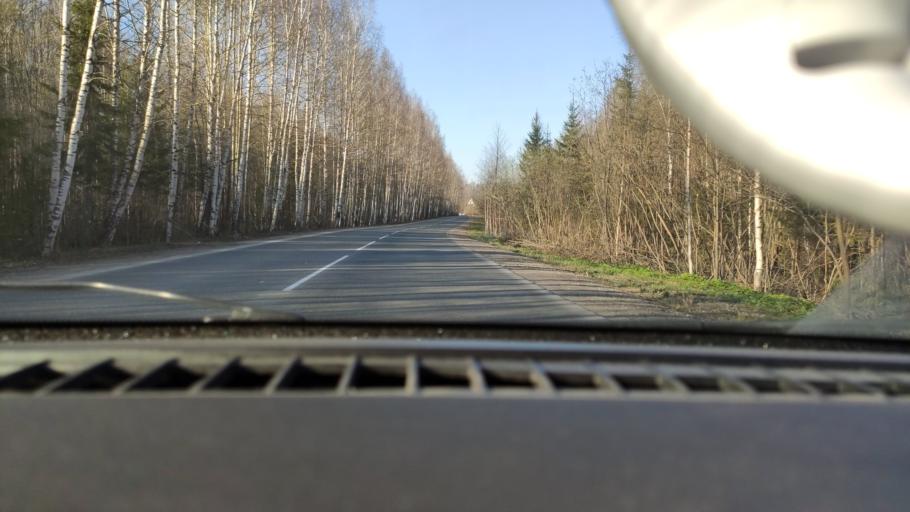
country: RU
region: Perm
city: Polazna
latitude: 58.1207
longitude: 56.4313
